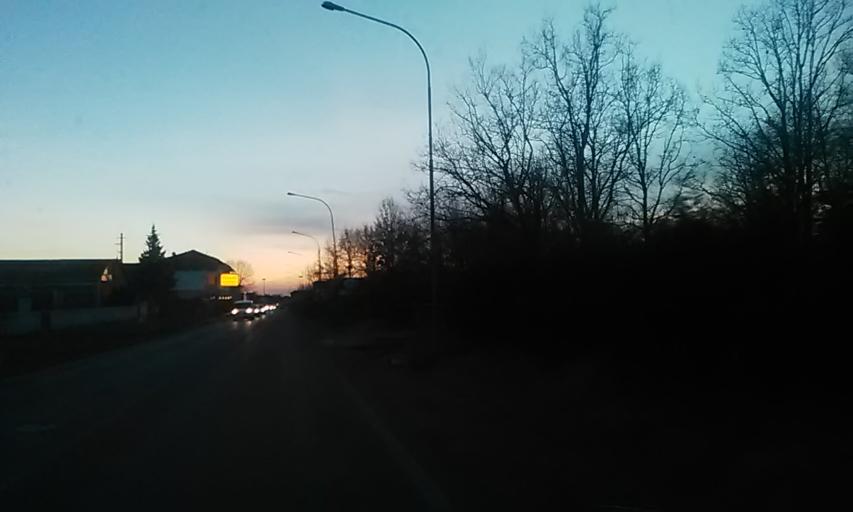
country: IT
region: Piedmont
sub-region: Provincia di Biella
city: Brusnengo
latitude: 45.5672
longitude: 8.2465
